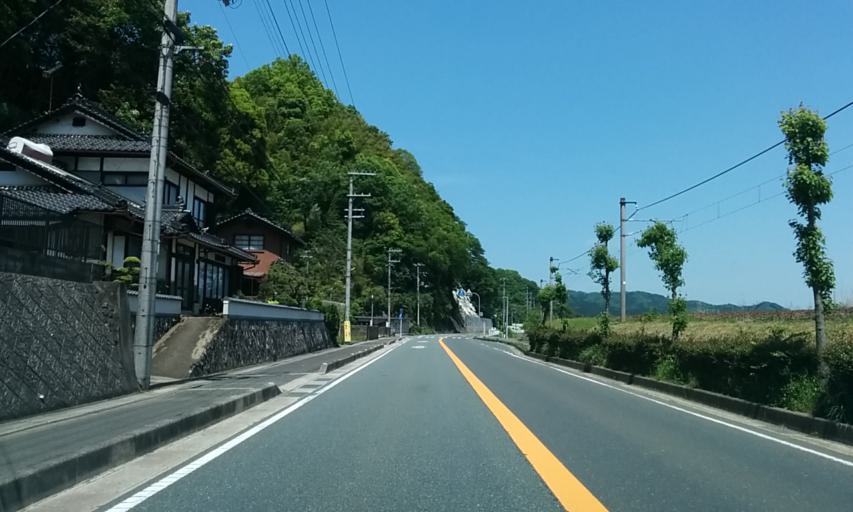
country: JP
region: Kyoto
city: Fukuchiyama
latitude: 35.3768
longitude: 135.1335
